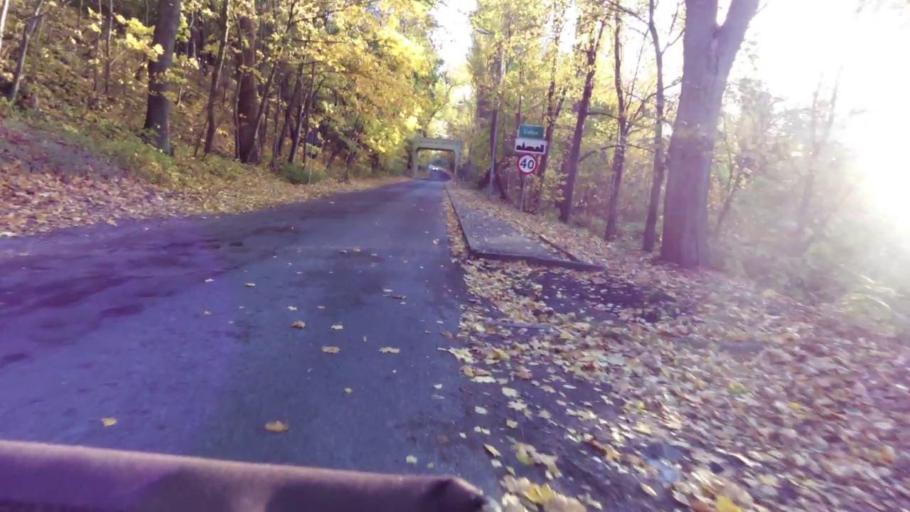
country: PL
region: West Pomeranian Voivodeship
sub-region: Powiat kamienski
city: Miedzyzdroje
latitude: 53.8764
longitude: 14.4280
